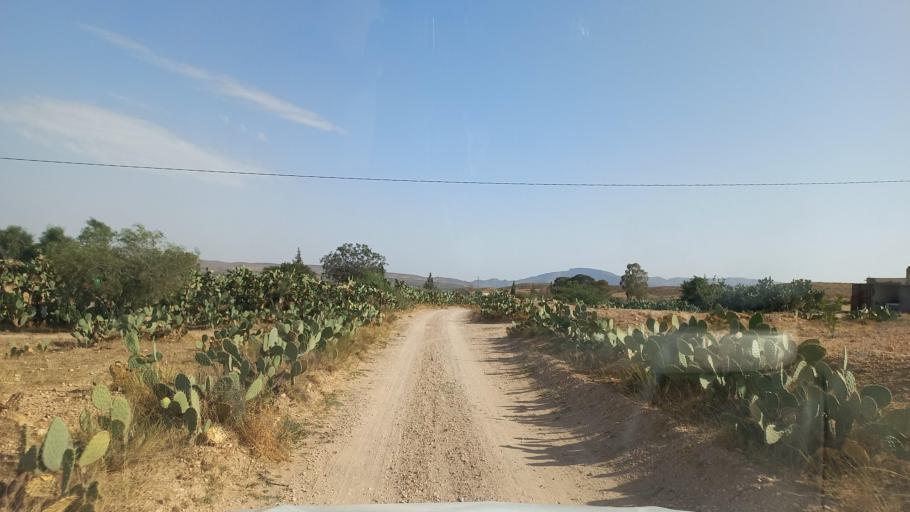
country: TN
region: Al Qasrayn
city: Kasserine
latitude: 35.2538
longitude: 8.9282
